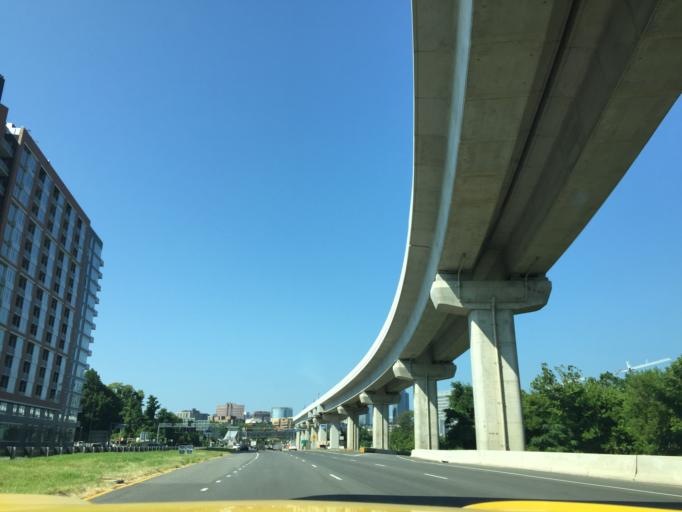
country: US
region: Virginia
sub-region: Fairfax County
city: Pimmit Hills
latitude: 38.9280
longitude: -77.2046
